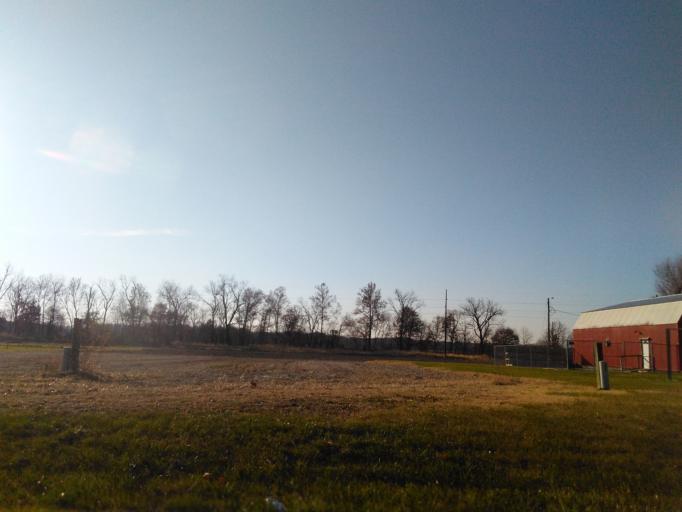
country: US
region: Illinois
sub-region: Madison County
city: Saint Jacob
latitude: 38.7161
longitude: -89.8198
